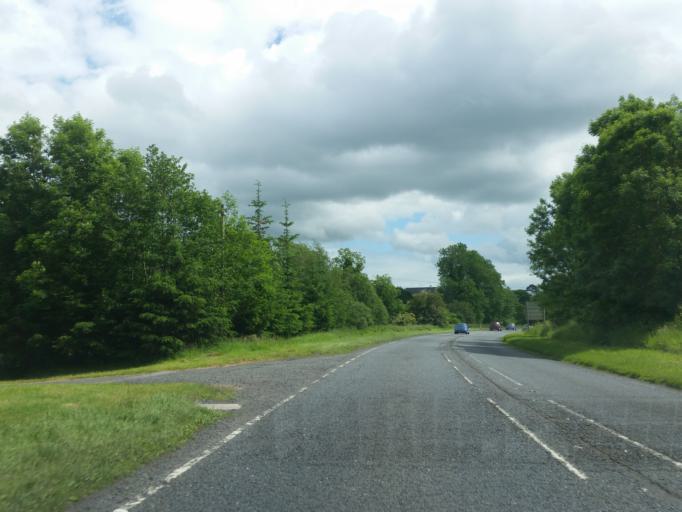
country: IE
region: Ulster
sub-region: County Monaghan
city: Monaghan
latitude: 54.4710
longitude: -7.0502
